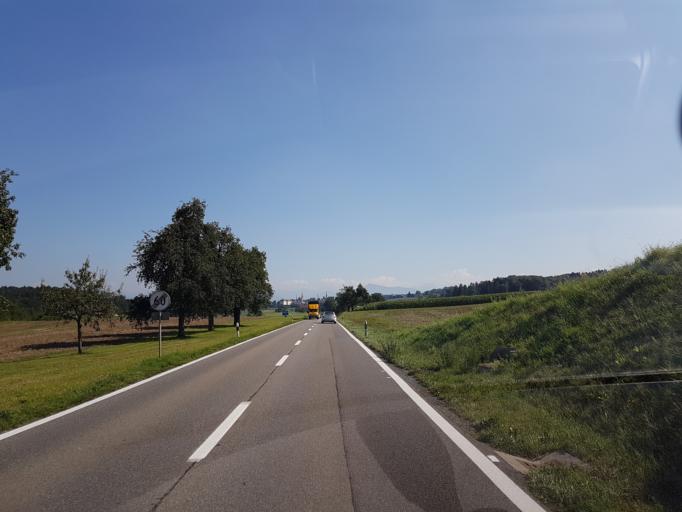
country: CH
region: Aargau
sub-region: Bezirk Muri
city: Muri
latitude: 47.2933
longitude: 8.3210
